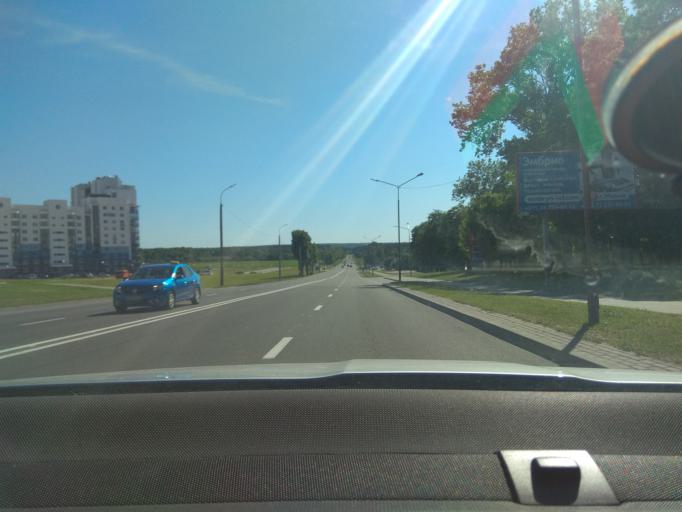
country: BY
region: Grodnenskaya
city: Hrodna
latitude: 53.6481
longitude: 23.7800
